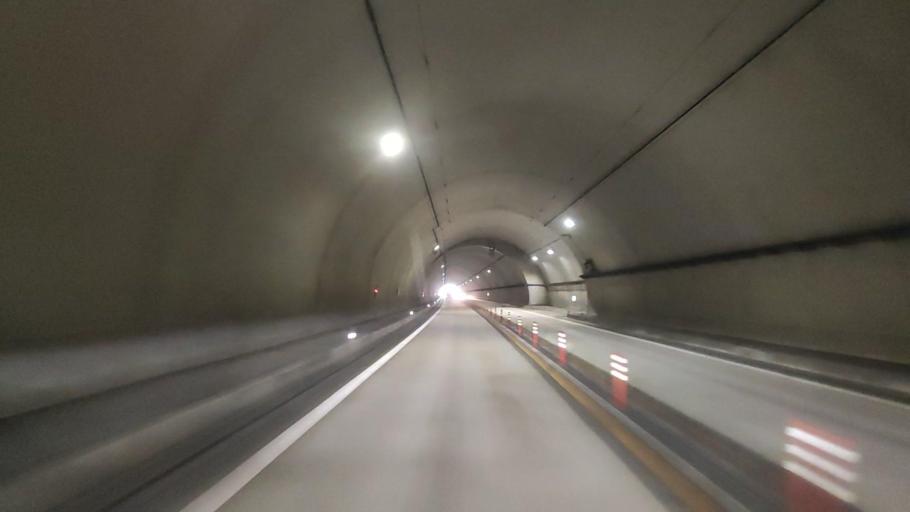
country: JP
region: Wakayama
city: Tanabe
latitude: 33.5638
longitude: 135.4997
